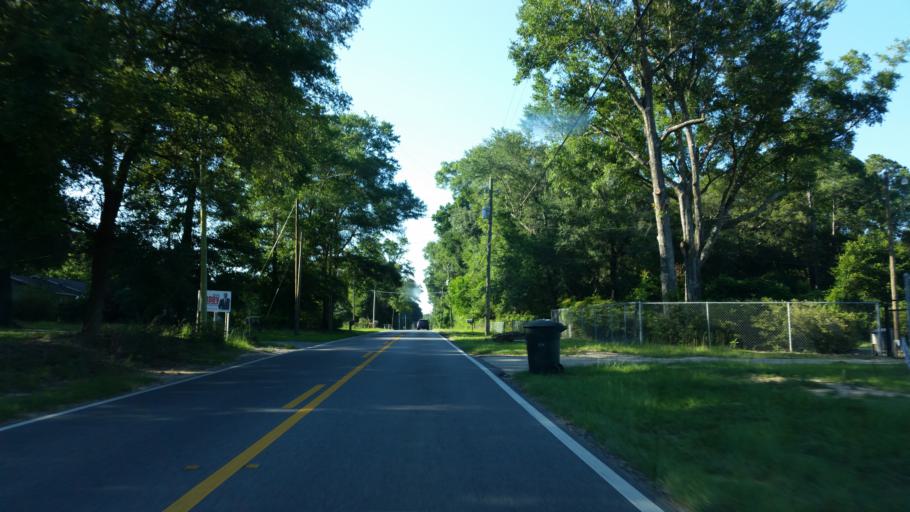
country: US
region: Florida
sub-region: Escambia County
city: Bellview
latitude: 30.5256
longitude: -87.3809
